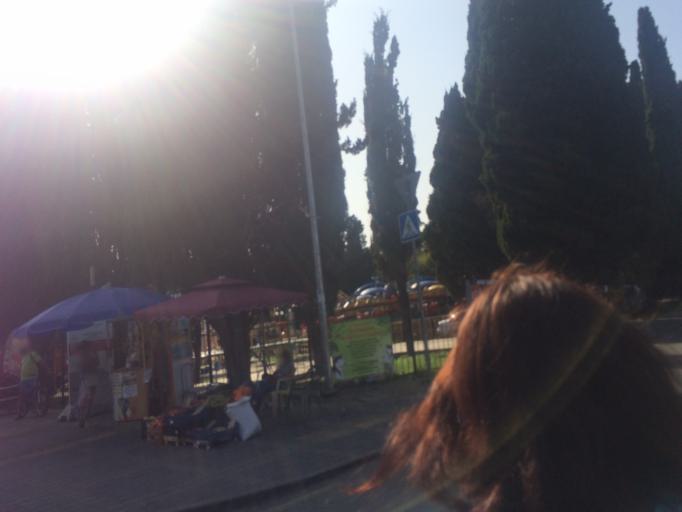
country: RU
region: Krasnodarskiy
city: Adler
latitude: 43.3912
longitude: 39.9858
